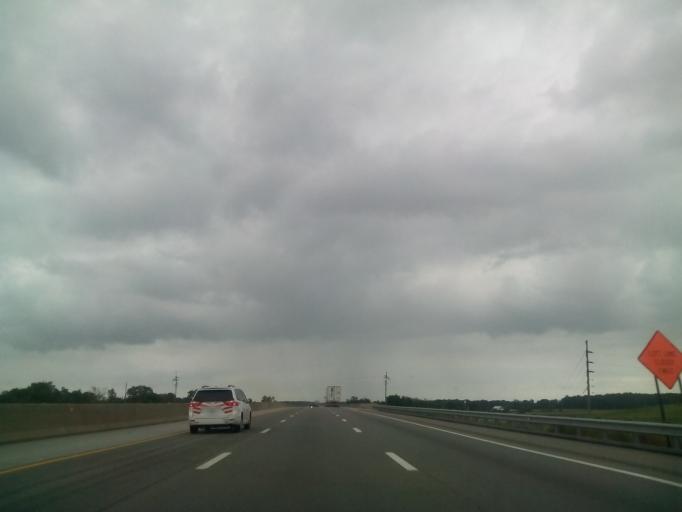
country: US
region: Ohio
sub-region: Sandusky County
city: Clyde
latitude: 41.3741
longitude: -82.9805
